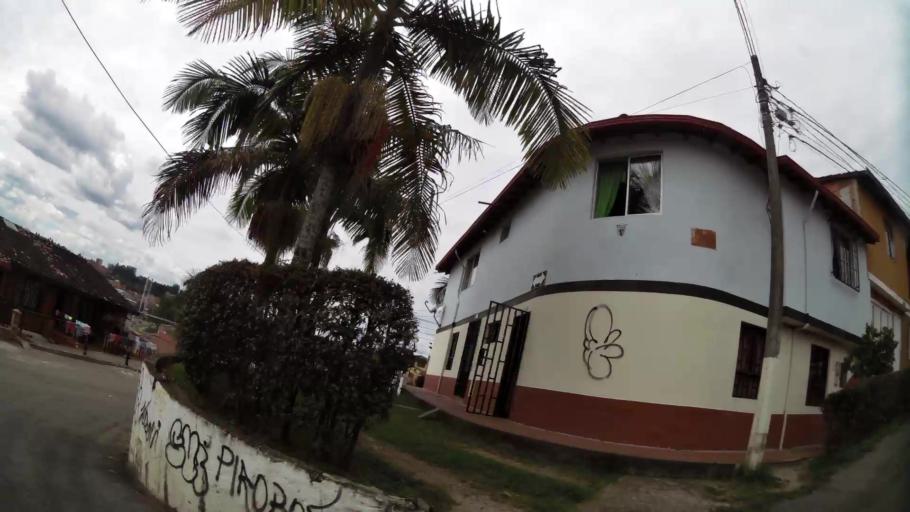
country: CO
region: Antioquia
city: Rionegro
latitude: 6.1521
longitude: -75.3656
